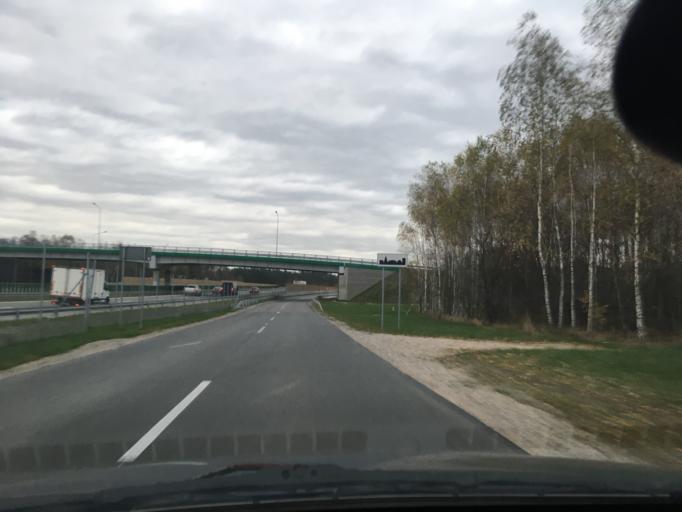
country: PL
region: Lodz Voivodeship
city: Zabia Wola
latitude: 52.0425
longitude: 20.7021
